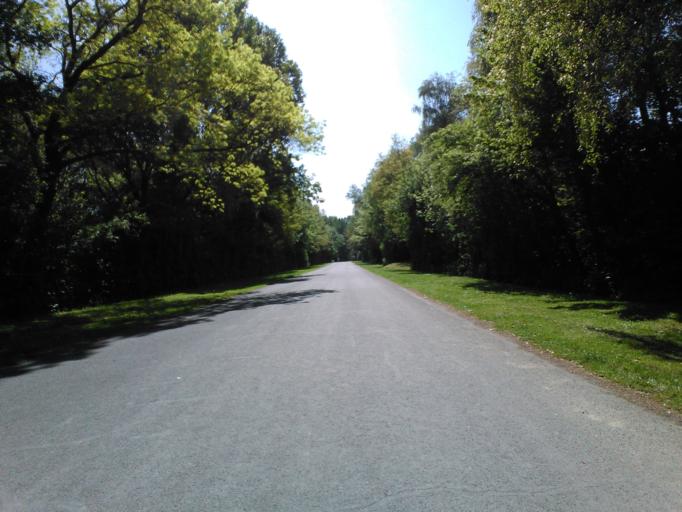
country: NL
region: South Holland
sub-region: Gemeente Sliedrecht
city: Sliedrecht
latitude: 51.8139
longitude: 4.7665
